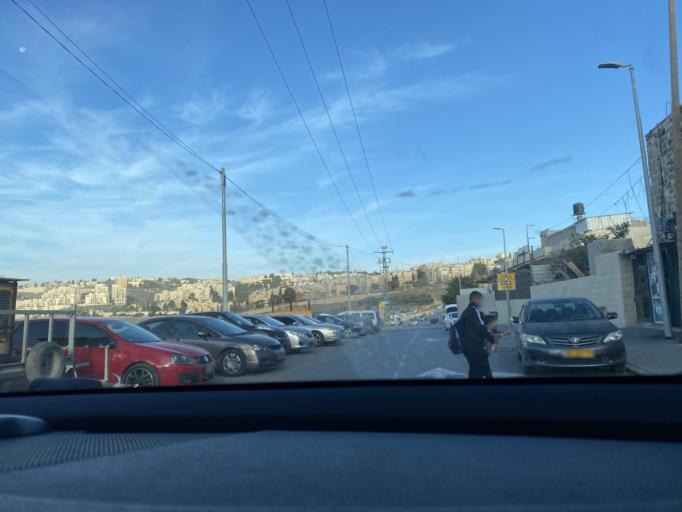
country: PS
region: West Bank
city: Ash Shaykh Sa`d
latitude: 31.7407
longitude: 35.2416
